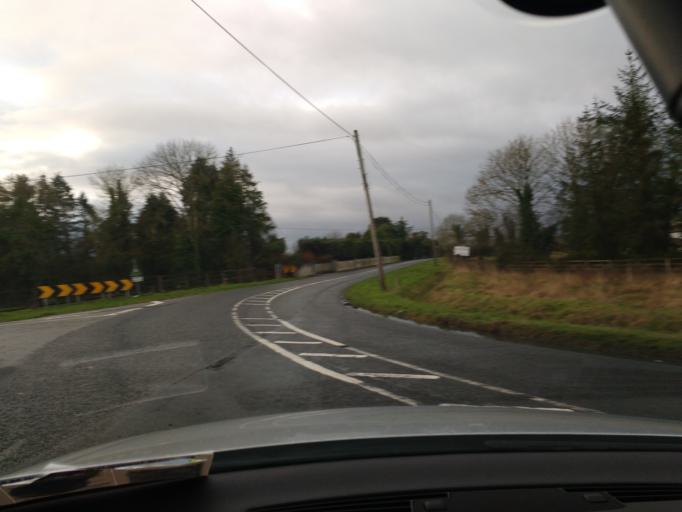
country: IE
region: Munster
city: Thurles
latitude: 52.6367
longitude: -7.8460
